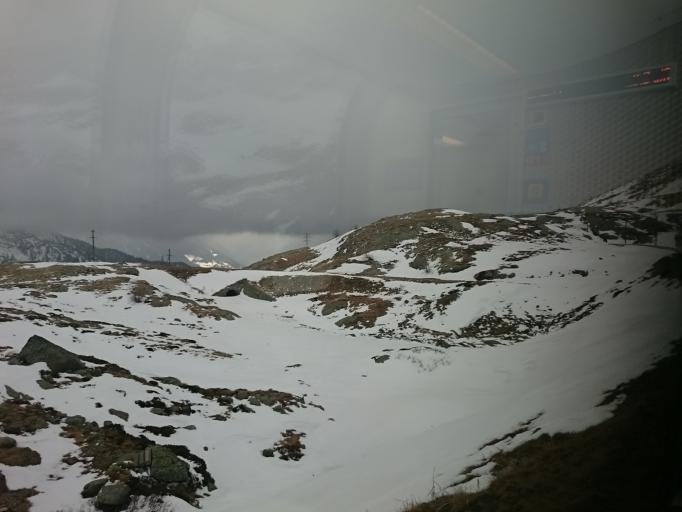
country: CH
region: Grisons
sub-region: Bernina District
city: Poschiavo
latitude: 46.3911
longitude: 10.0325
